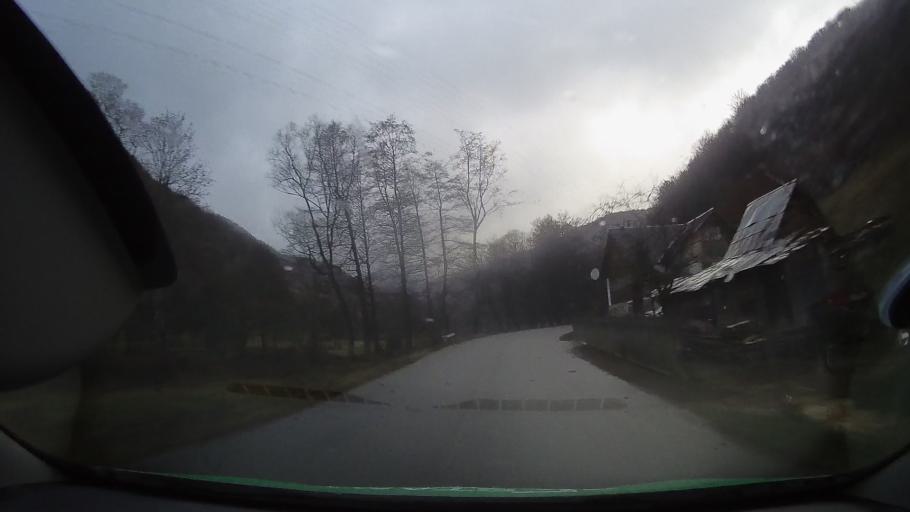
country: RO
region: Hunedoara
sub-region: Comuna Ribita
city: Ribita
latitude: 46.2731
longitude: 22.7415
